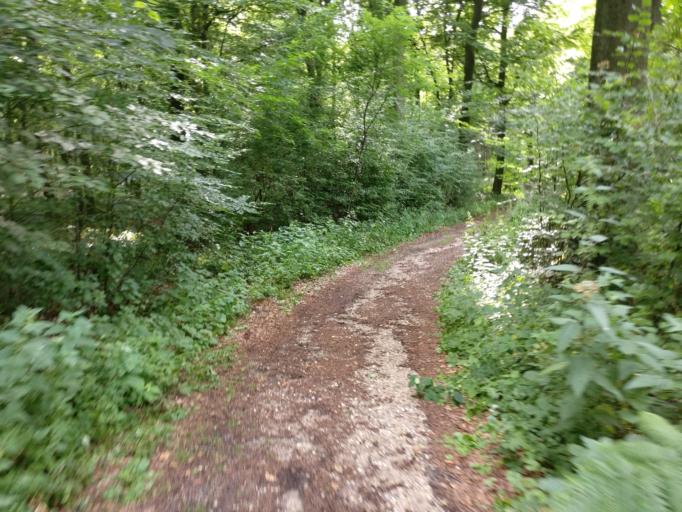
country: DE
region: North Rhine-Westphalia
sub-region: Regierungsbezirk Dusseldorf
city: Duisburg
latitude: 51.4152
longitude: 6.8014
